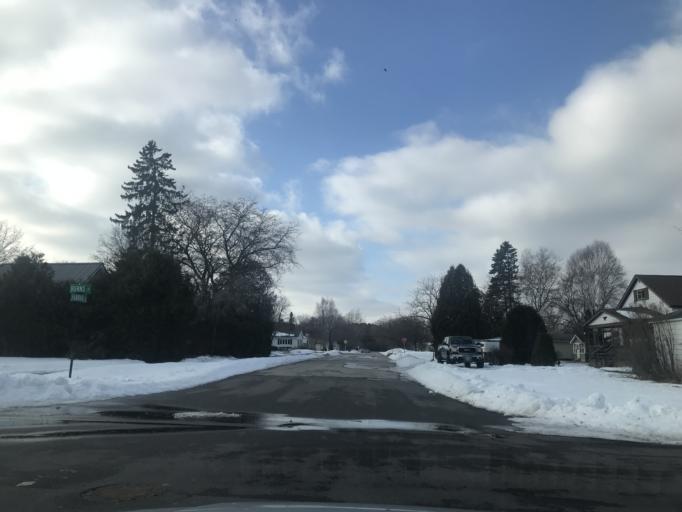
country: US
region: Wisconsin
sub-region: Marinette County
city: Marinette
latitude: 45.1012
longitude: -87.6461
